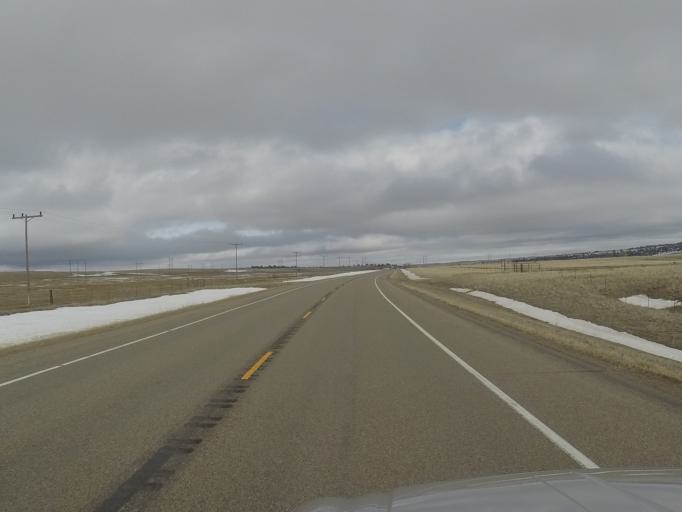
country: US
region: Montana
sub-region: Golden Valley County
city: Ryegate
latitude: 46.3285
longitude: -109.4701
